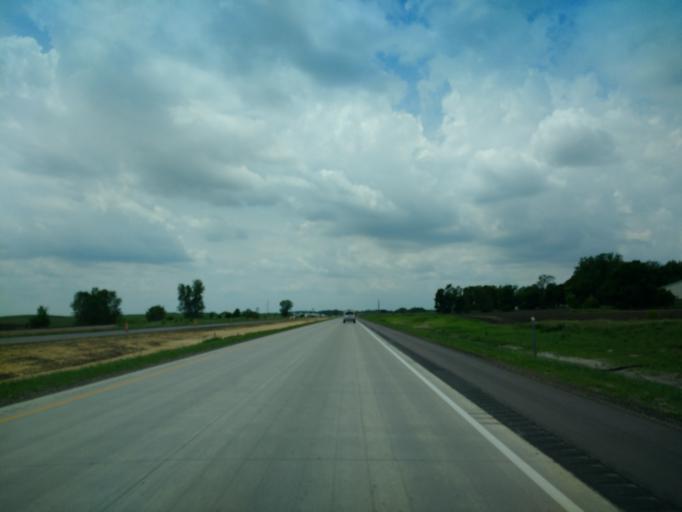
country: US
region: Minnesota
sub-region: Cottonwood County
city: Windom
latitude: 43.8939
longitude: -95.0842
